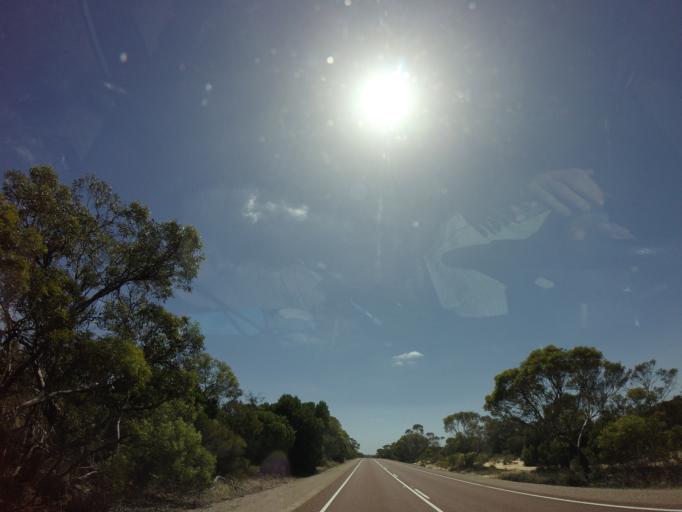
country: AU
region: South Australia
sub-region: Kimba
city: Caralue
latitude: -33.2205
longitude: 136.3395
